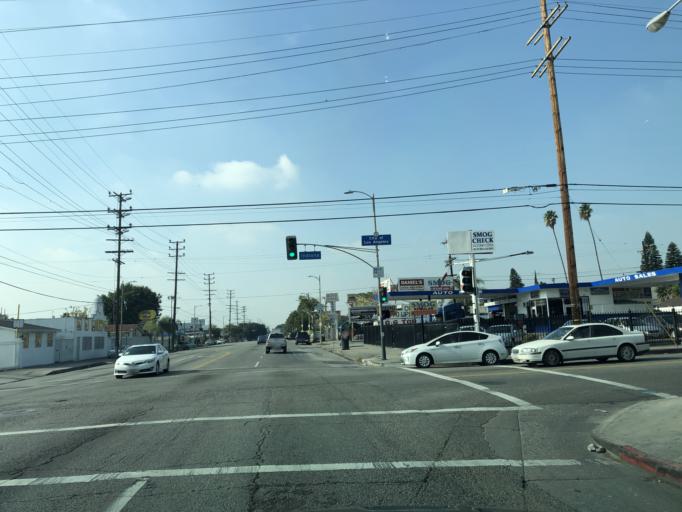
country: US
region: California
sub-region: Los Angeles County
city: Boyle Heights
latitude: 34.0189
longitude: -118.1921
